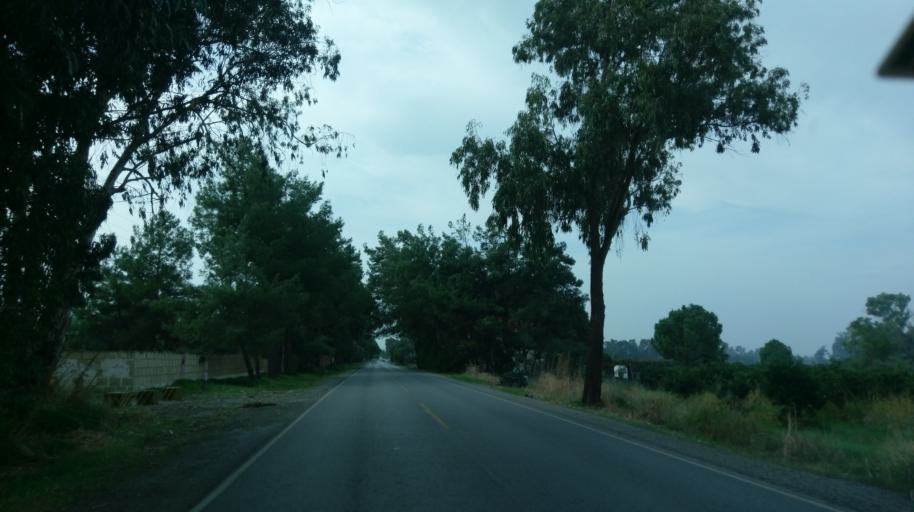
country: CY
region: Lefkosia
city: Lefka
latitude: 35.1565
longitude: 32.8926
